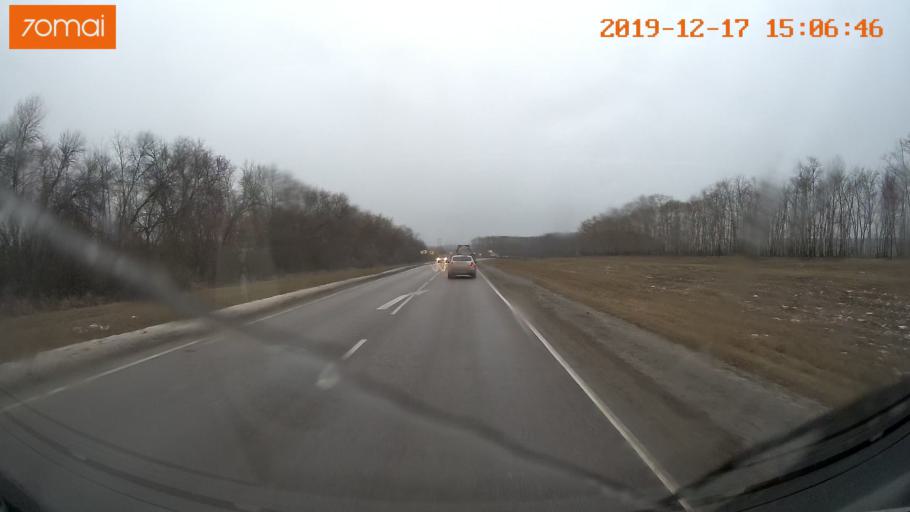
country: RU
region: Rjazan
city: Mikhaylov
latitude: 54.2566
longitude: 39.0945
